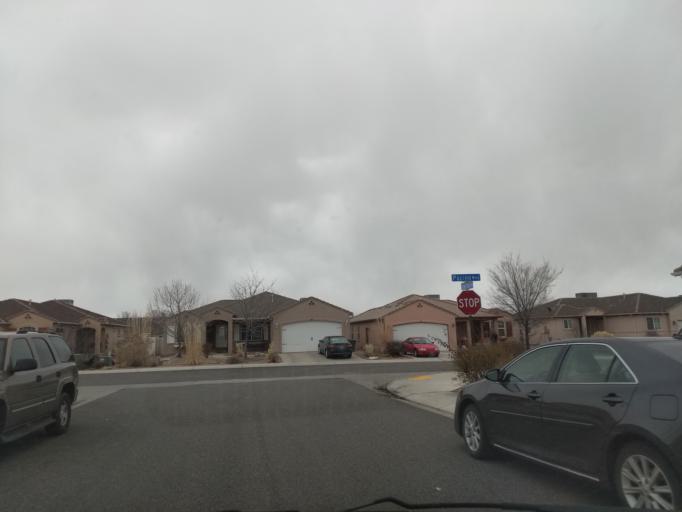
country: US
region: Colorado
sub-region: Mesa County
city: Fruitvale
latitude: 39.0895
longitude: -108.5215
